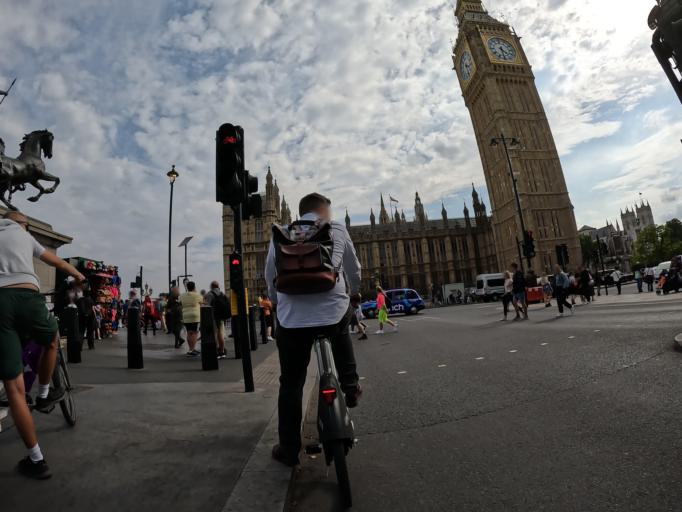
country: GB
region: England
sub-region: Kent
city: Halstead
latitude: 51.3403
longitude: 0.1248
